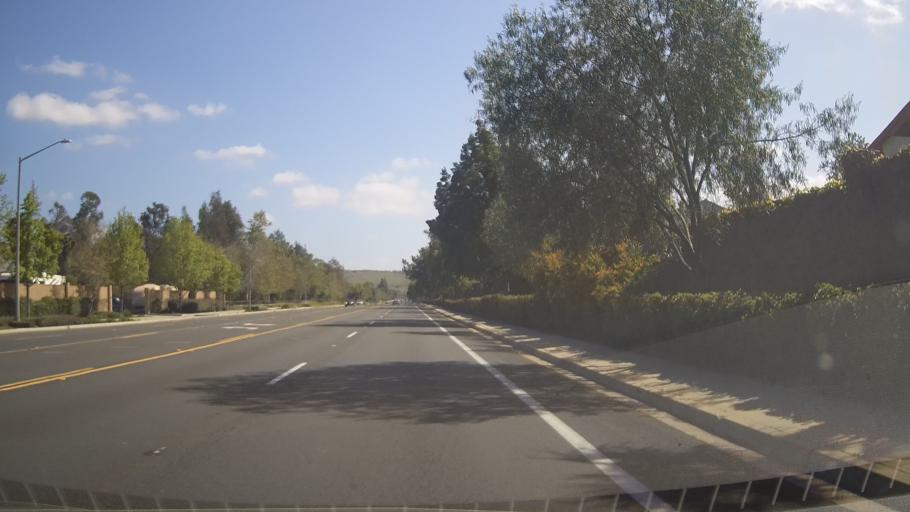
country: US
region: California
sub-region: San Diego County
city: Poway
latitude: 32.9704
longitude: -117.0407
